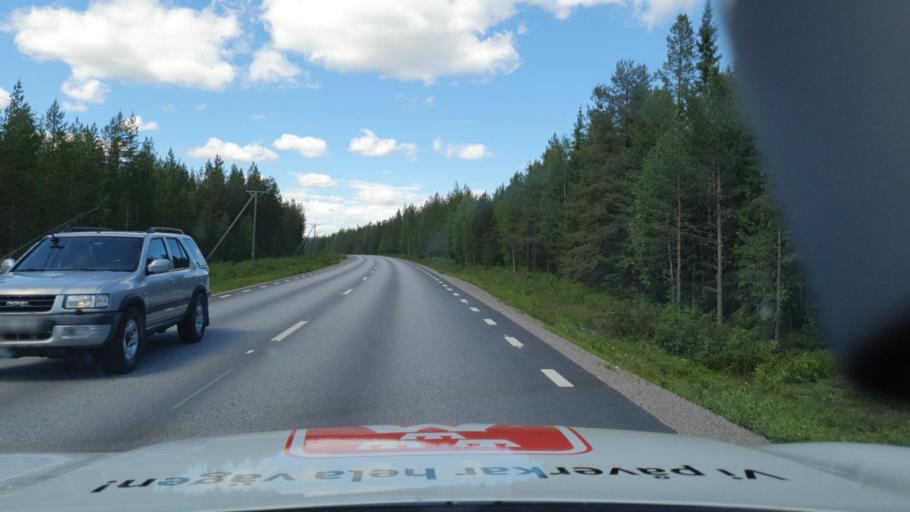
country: SE
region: Vaesterbotten
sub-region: Skelleftea Kommun
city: Boliden
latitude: 64.9269
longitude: 20.3191
